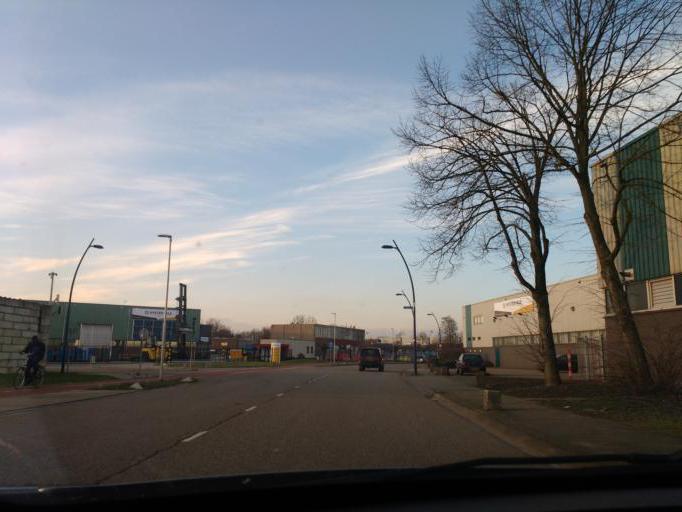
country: NL
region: Gelderland
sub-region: Gemeente Nijmegen
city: Nijmegen
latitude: 51.8513
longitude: 5.8283
